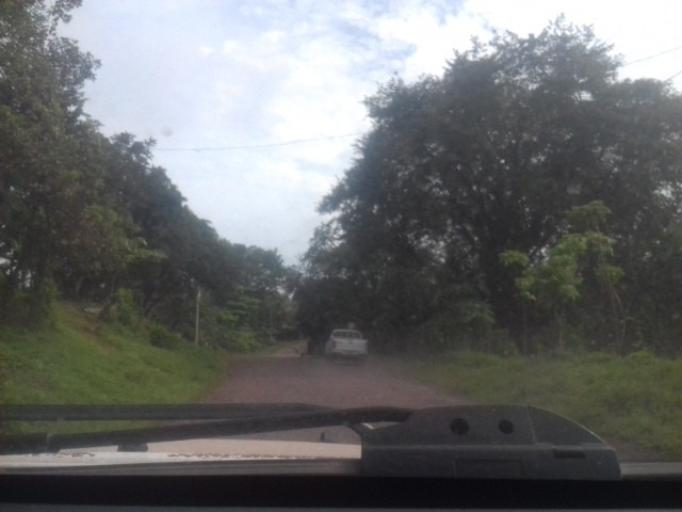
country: NI
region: Atlantico Norte (RAAN)
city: Waslala
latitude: 13.4353
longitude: -85.3096
